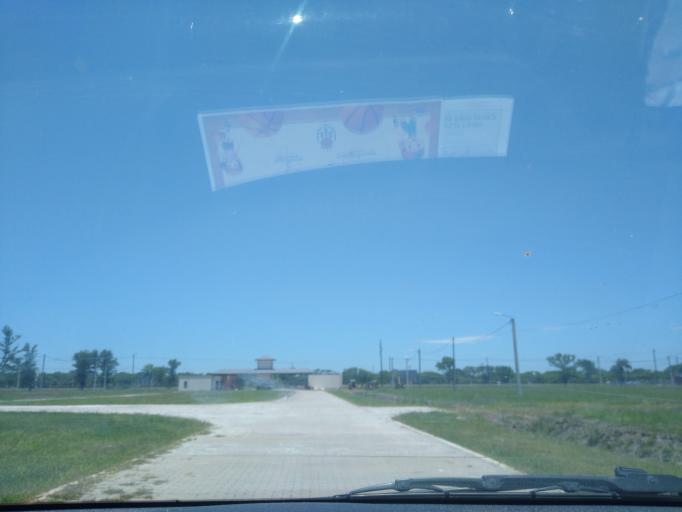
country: AR
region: Chaco
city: Makalle
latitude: -27.2507
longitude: -59.1633
